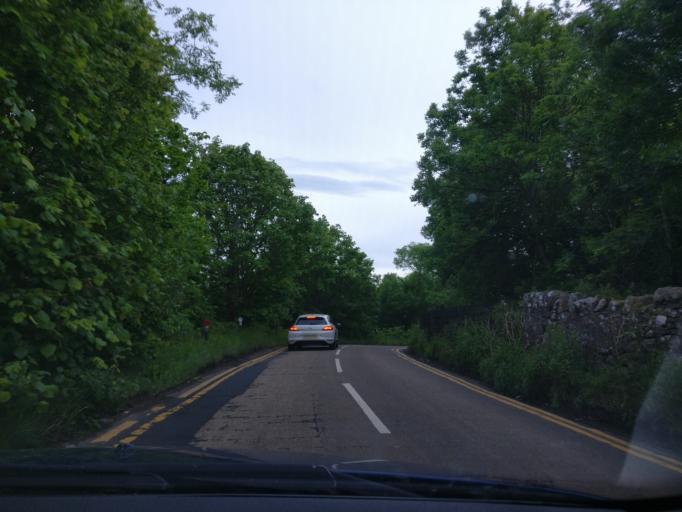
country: GB
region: Scotland
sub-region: West Lothian
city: Seafield
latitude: 55.9246
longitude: -3.1378
